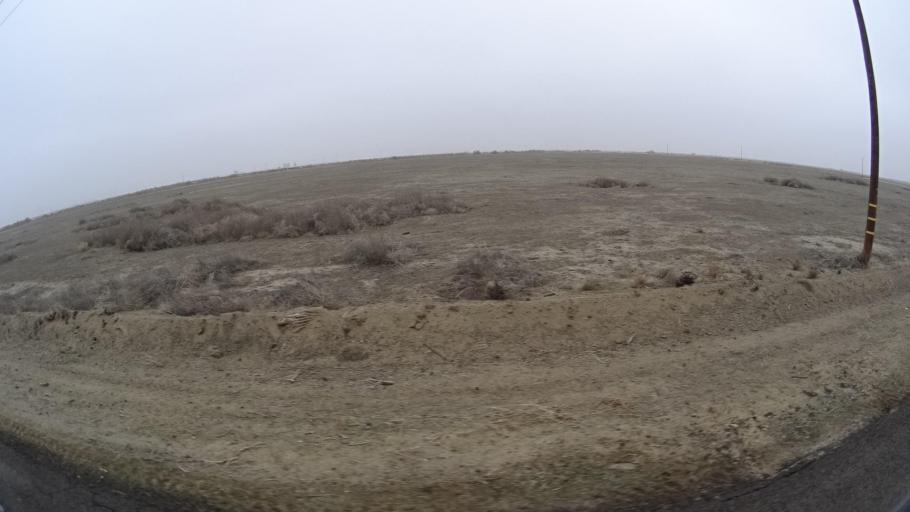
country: US
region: California
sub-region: Kern County
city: Lost Hills
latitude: 35.5921
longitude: -119.5805
